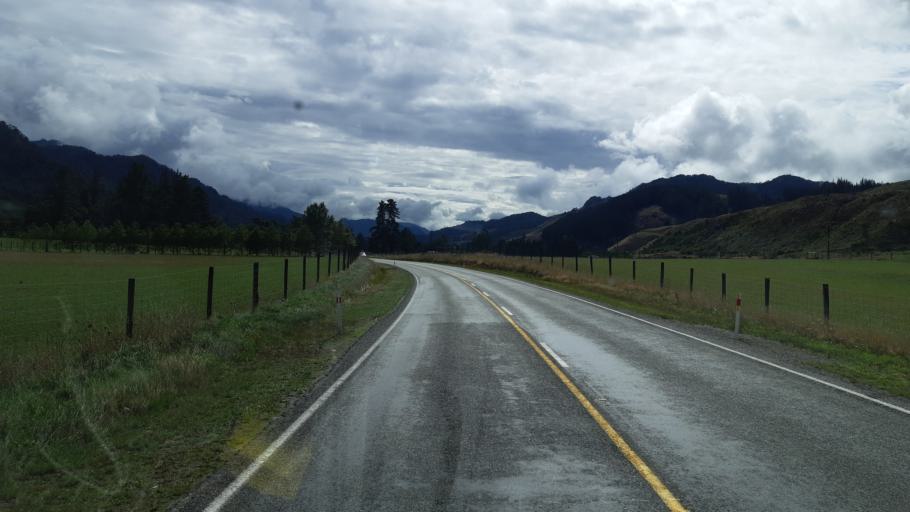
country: NZ
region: Tasman
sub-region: Tasman District
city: Wakefield
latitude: -41.7777
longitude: 172.3769
